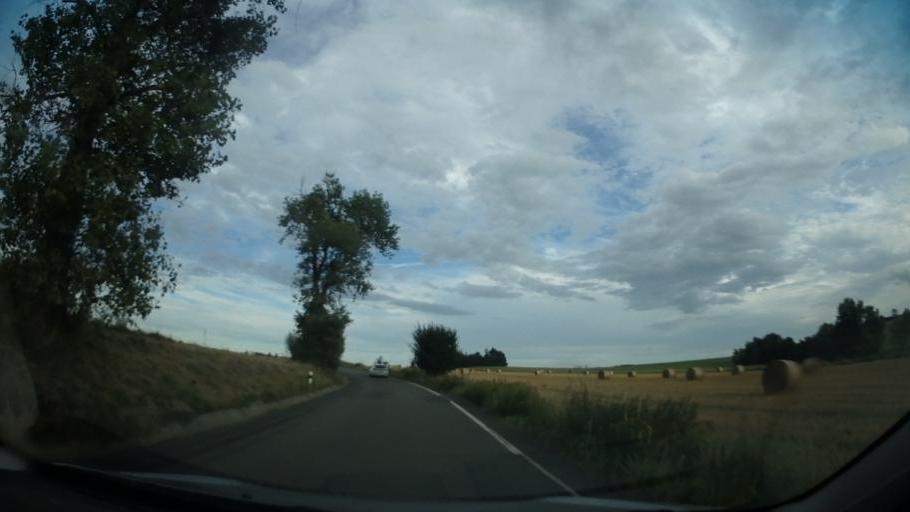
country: CZ
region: Olomoucky
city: Horni Stepanov
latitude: 49.5530
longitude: 16.7786
